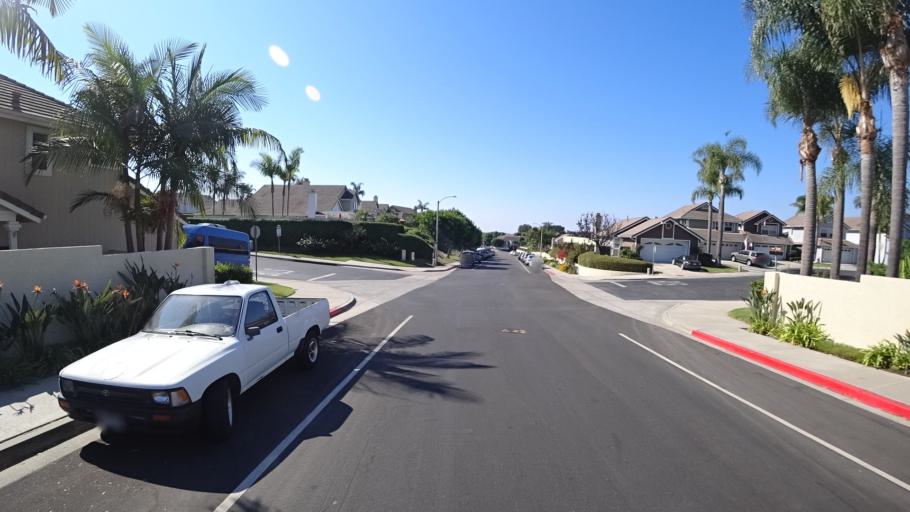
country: US
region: California
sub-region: Orange County
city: San Clemente
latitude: 33.4489
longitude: -117.6300
